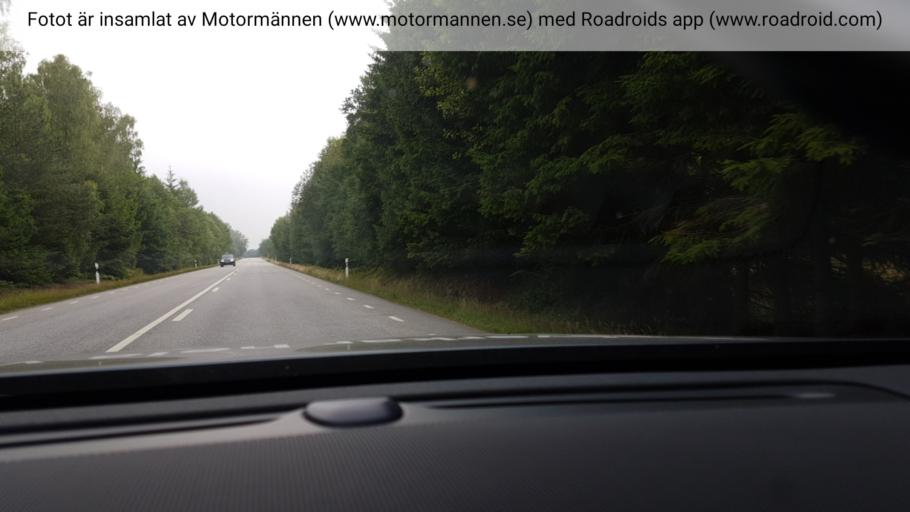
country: SE
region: Skane
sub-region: Hassleholms Kommun
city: Bjarnum
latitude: 56.2460
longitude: 13.7149
